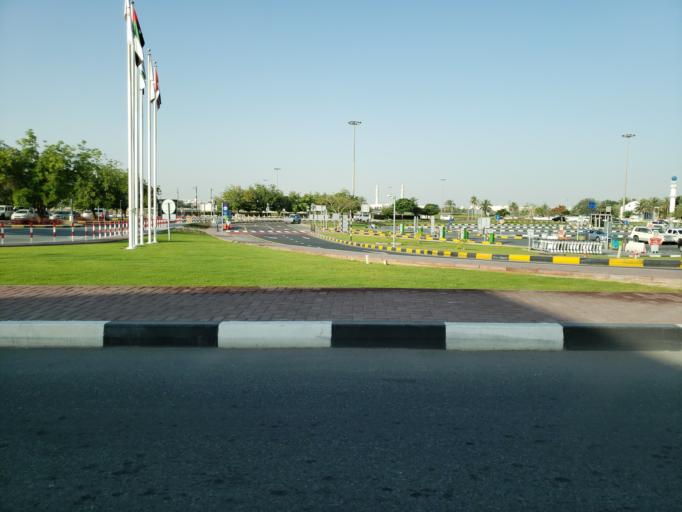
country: AE
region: Ash Shariqah
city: Sharjah
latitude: 25.3206
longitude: 55.5211
